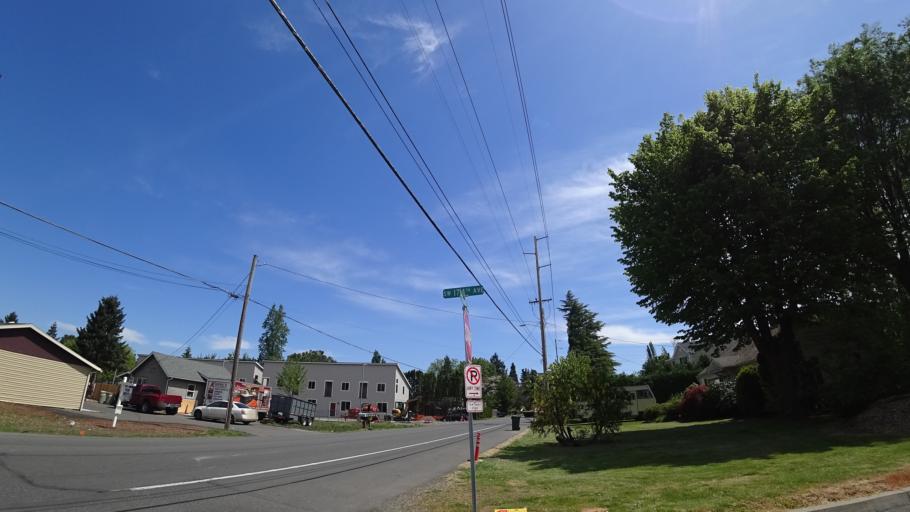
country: US
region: Oregon
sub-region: Washington County
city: Aloha
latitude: 45.4909
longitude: -122.8561
